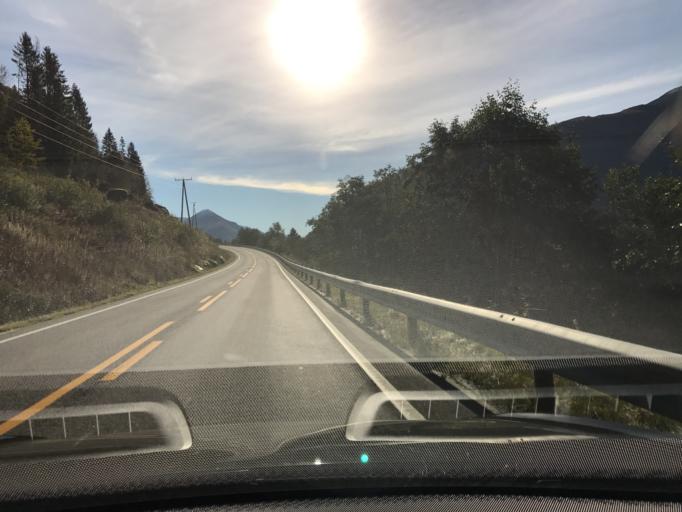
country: NO
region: Sogn og Fjordane
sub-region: Leikanger
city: Hermansverk
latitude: 61.4126
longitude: 6.7612
